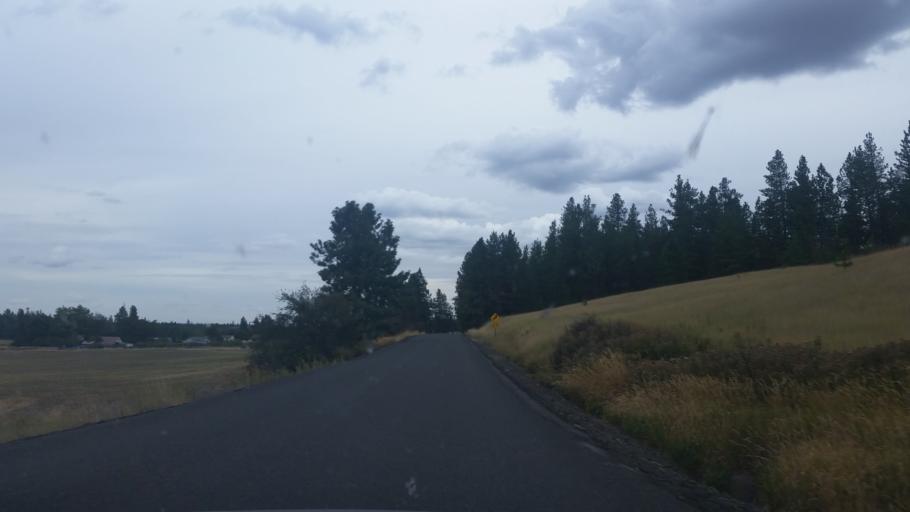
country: US
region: Washington
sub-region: Spokane County
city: Cheney
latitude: 47.5178
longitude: -117.5747
